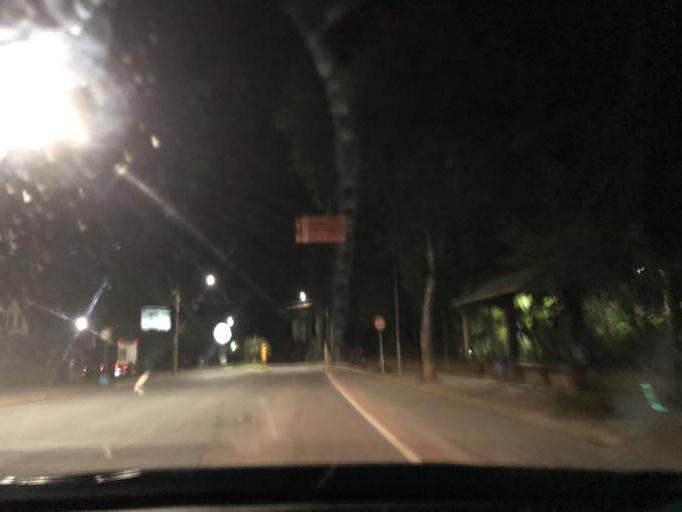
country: BR
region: Santa Catarina
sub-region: Jaragua Do Sul
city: Jaragua do Sul
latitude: -26.5136
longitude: -49.1238
